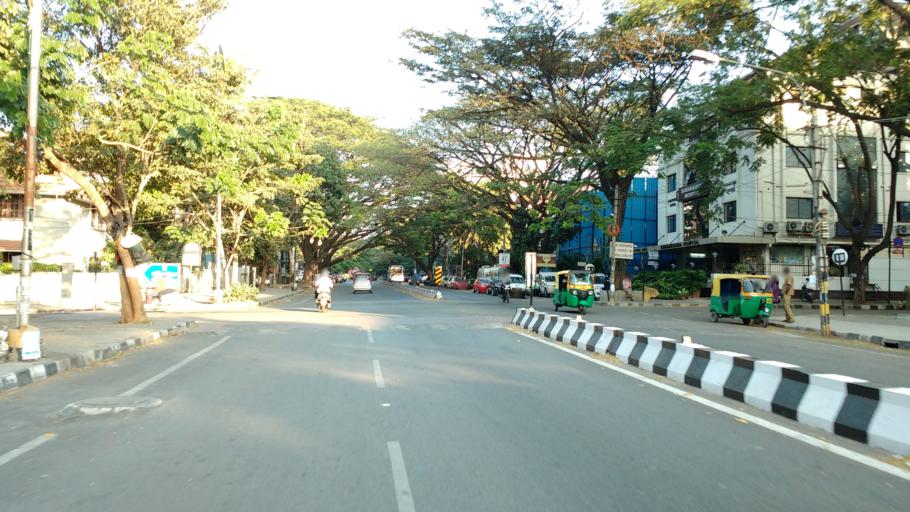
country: IN
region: Karnataka
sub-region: Bangalore Urban
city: Bangalore
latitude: 12.9368
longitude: 77.5825
